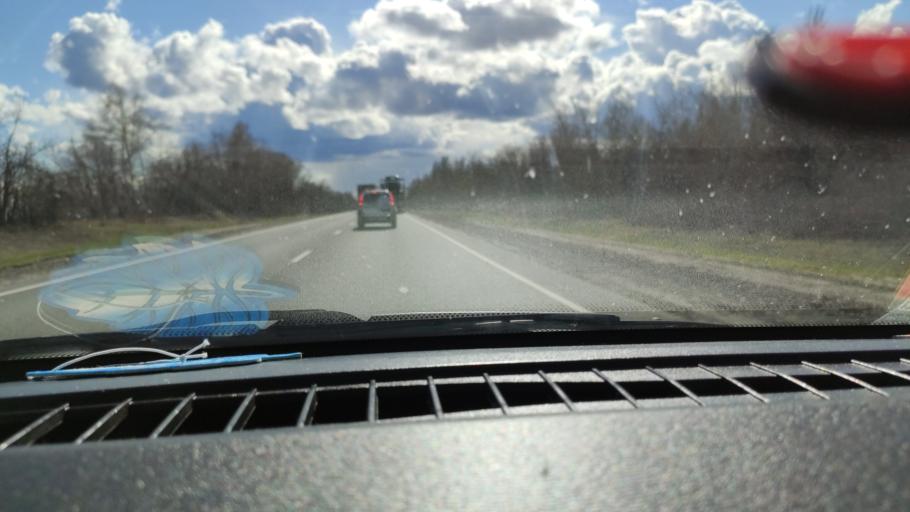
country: RU
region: Saratov
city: Khvalynsk
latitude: 52.5982
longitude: 48.1408
